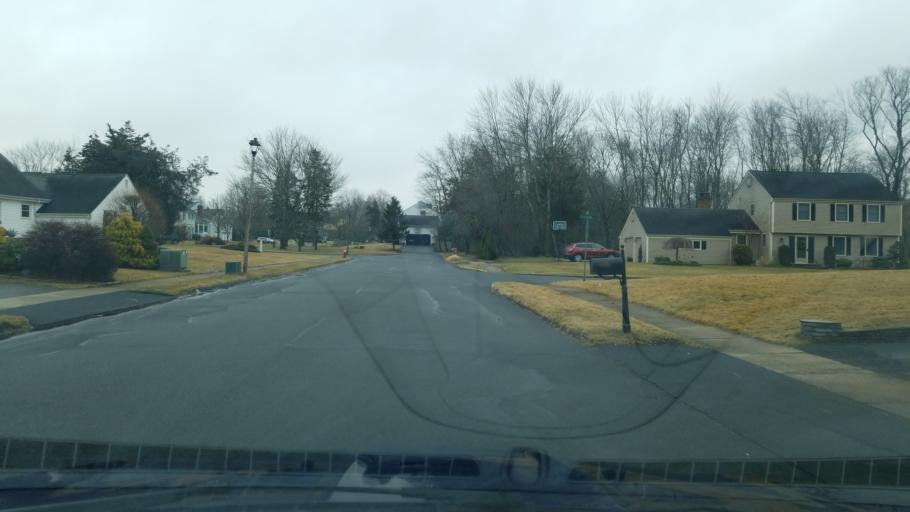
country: US
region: Connecticut
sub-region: Hartford County
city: Wethersfield
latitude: 41.6738
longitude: -72.6804
